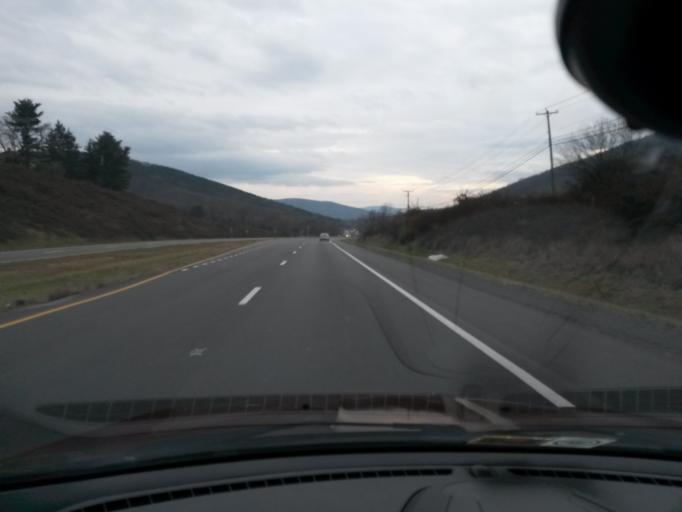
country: US
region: Virginia
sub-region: Botetourt County
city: Cloverdale
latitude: 37.3609
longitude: -79.8861
